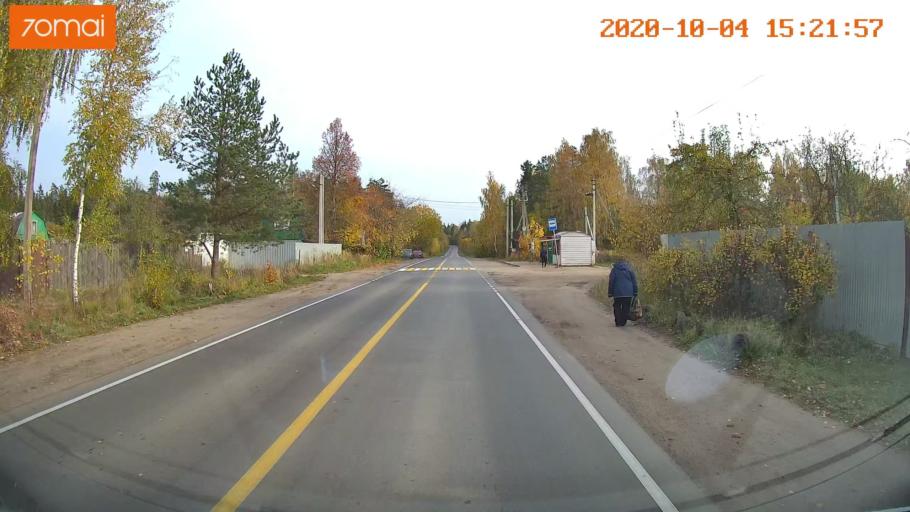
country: RU
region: Ivanovo
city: Bogorodskoye
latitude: 57.0833
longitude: 40.9287
